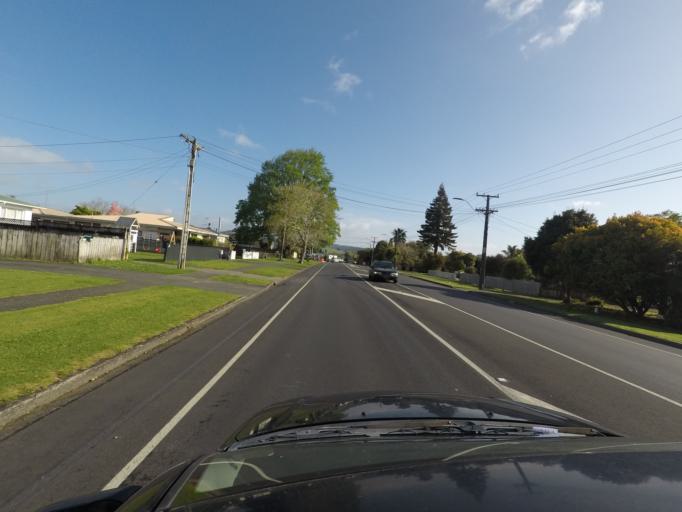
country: NZ
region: Northland
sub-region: Whangarei
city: Whangarei
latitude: -35.6886
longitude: 174.3269
